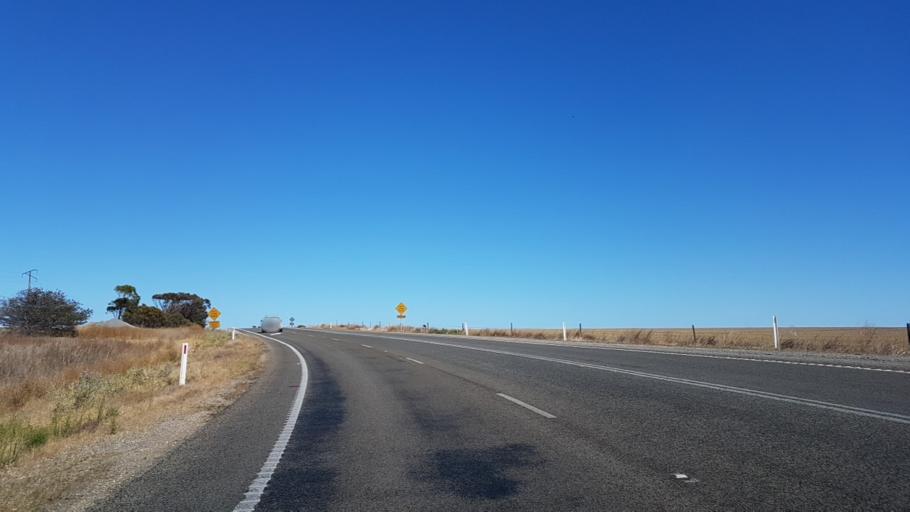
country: AU
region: South Australia
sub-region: Copper Coast
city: Kadina
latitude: -34.0612
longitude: 138.0456
